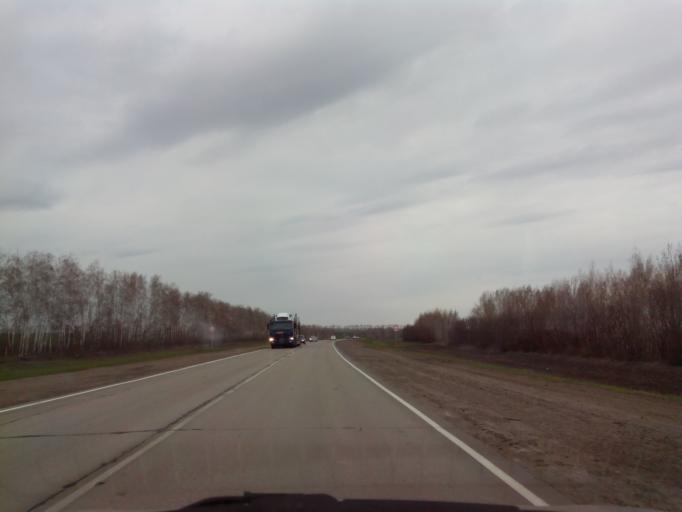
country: RU
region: Tambov
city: Znamenka
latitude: 52.4134
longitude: 41.3795
